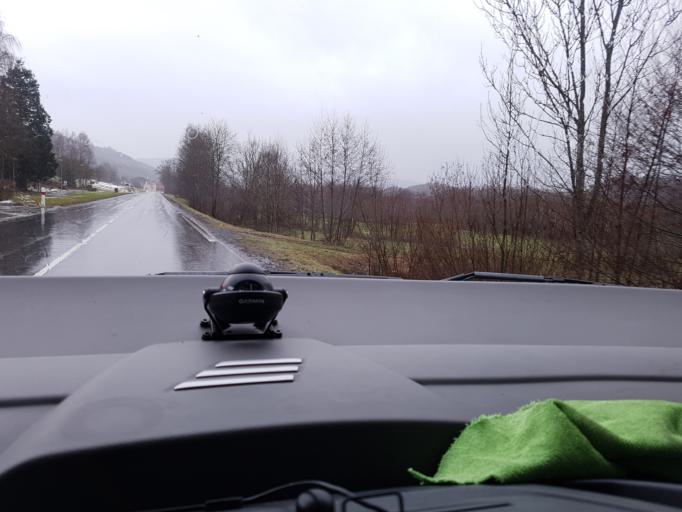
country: FR
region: Lorraine
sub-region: Departement des Vosges
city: Fraize
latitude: 48.1842
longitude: 6.9840
